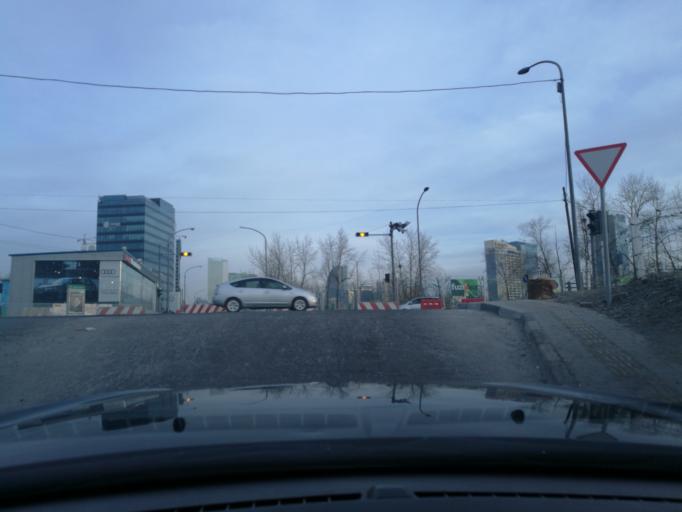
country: MN
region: Ulaanbaatar
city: Ulaanbaatar
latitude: 47.9079
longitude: 106.9152
